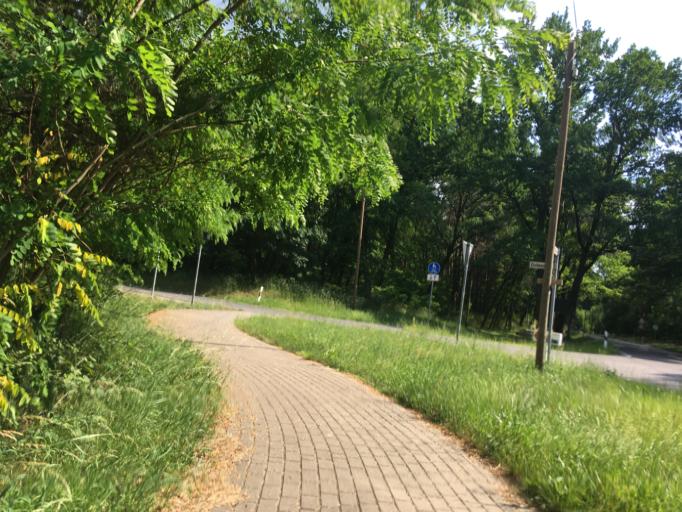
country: DE
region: Brandenburg
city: Furstenwalde
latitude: 52.3978
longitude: 14.0954
